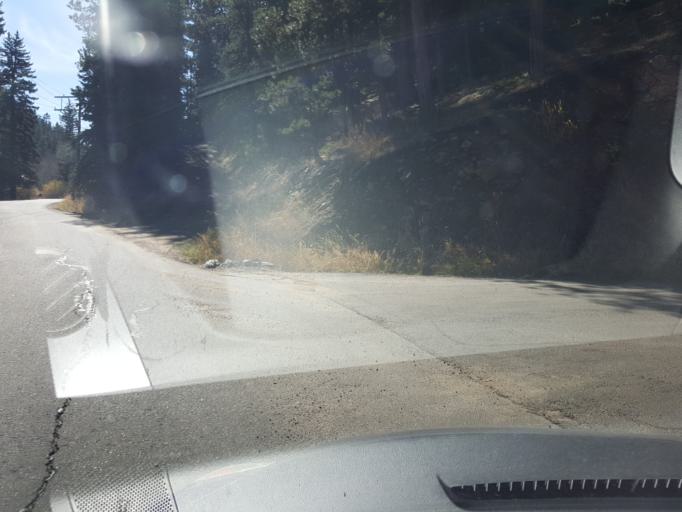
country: US
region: Colorado
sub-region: Jefferson County
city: Evergreen
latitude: 39.5879
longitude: -105.3440
